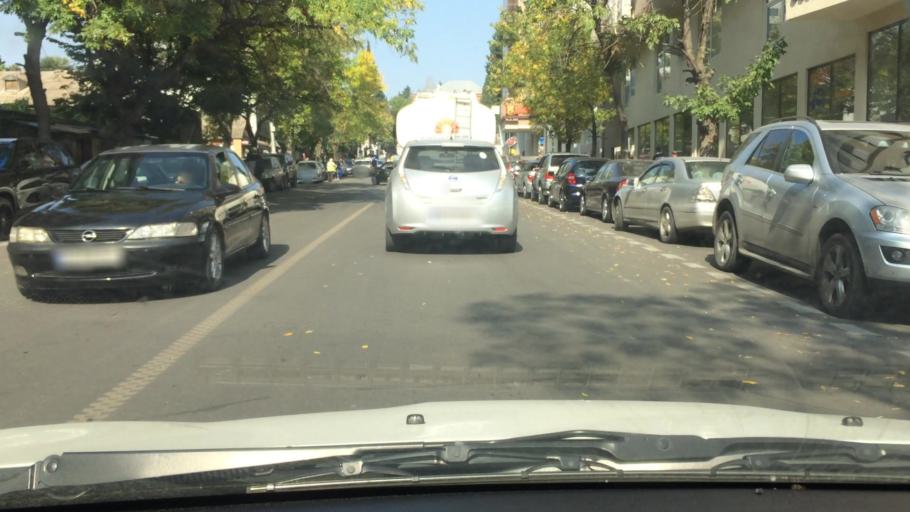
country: GE
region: T'bilisi
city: Tbilisi
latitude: 41.6893
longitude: 44.8278
